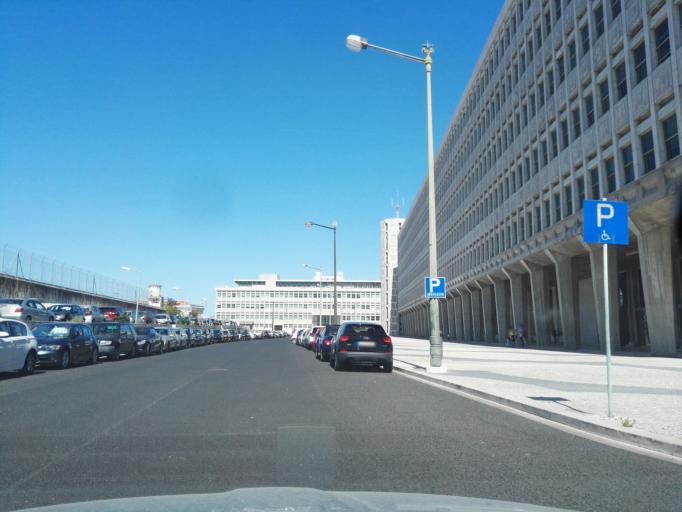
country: PT
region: Lisbon
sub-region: Lisbon
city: Lisbon
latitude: 38.7314
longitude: -9.1570
